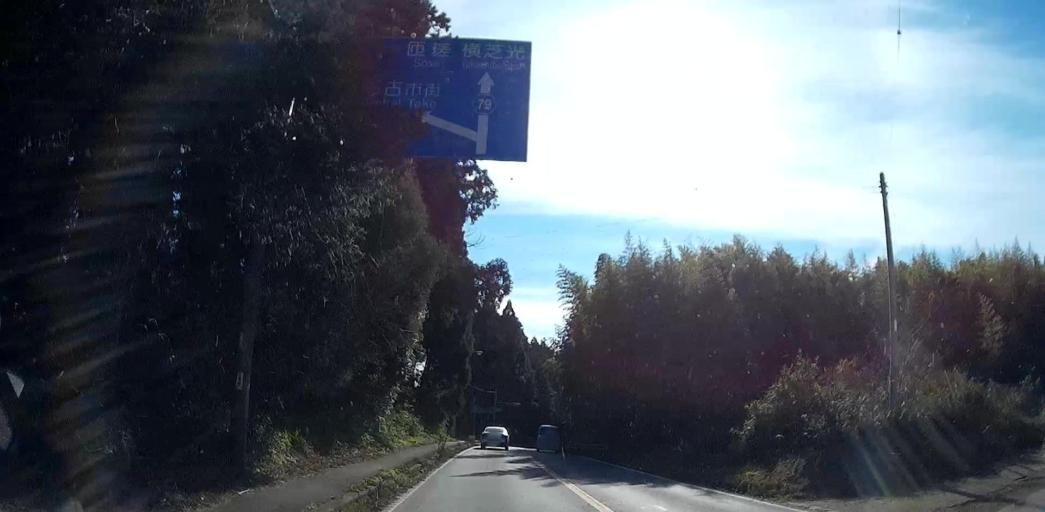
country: JP
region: Chiba
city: Yokaichiba
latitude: 35.7497
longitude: 140.4572
